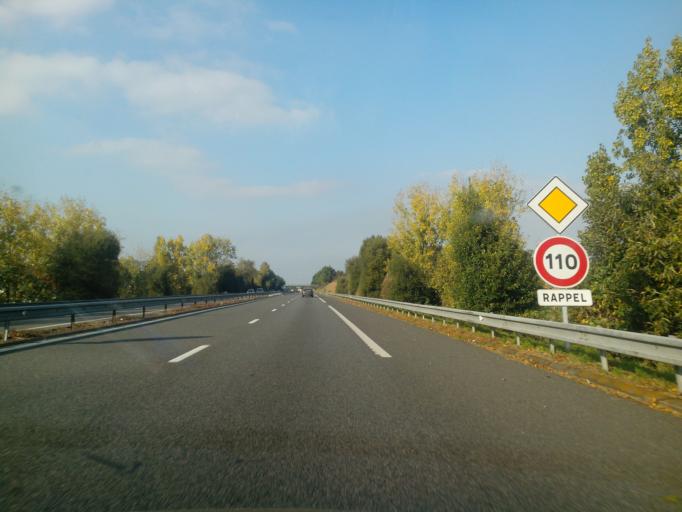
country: FR
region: Brittany
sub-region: Departement du Morbihan
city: Malestroit
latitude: 47.8575
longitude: -2.4174
